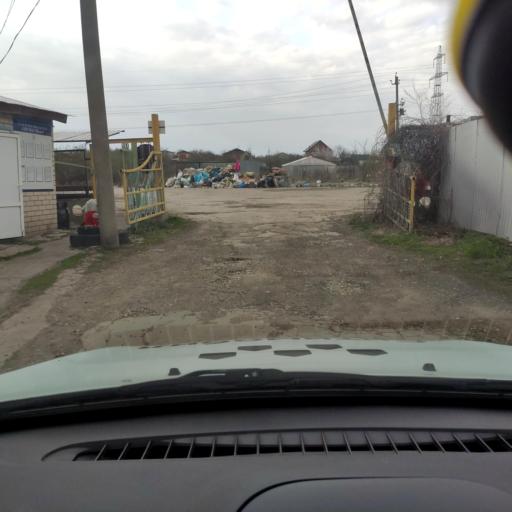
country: RU
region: Samara
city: Mezhdurechensk
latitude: 53.2481
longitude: 49.1482
